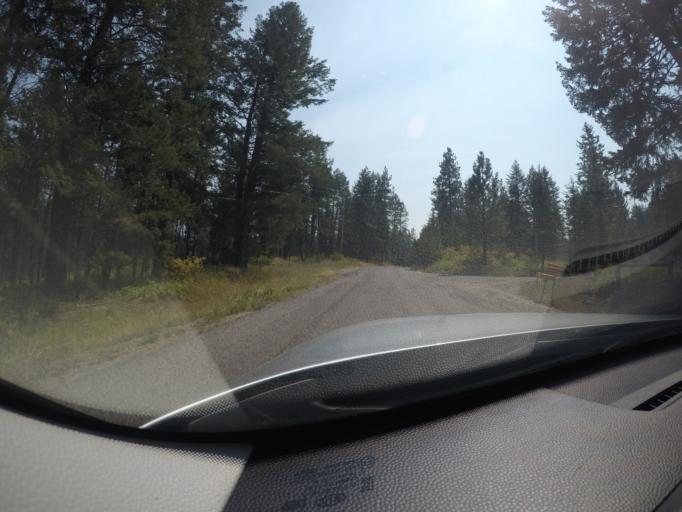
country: US
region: Montana
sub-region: Lake County
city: Polson
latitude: 47.7849
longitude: -114.1746
